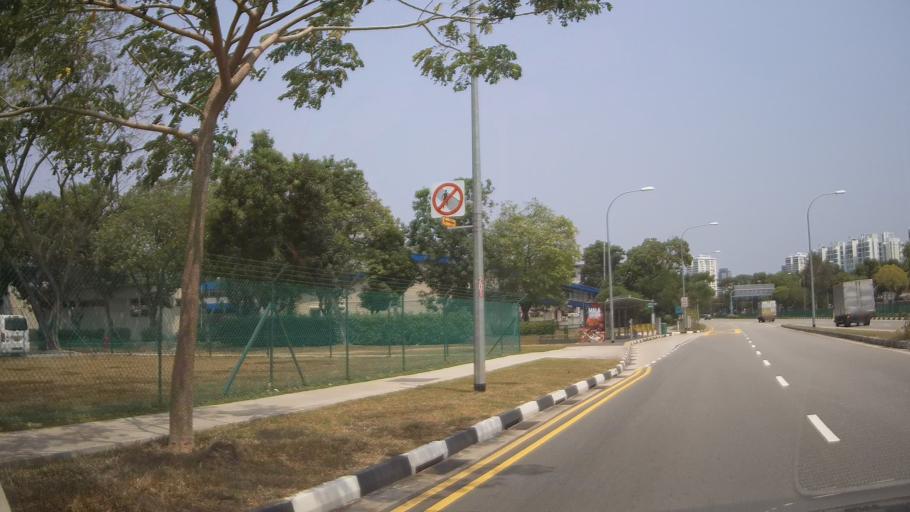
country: SG
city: Singapore
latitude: 1.3120
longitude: 103.7550
